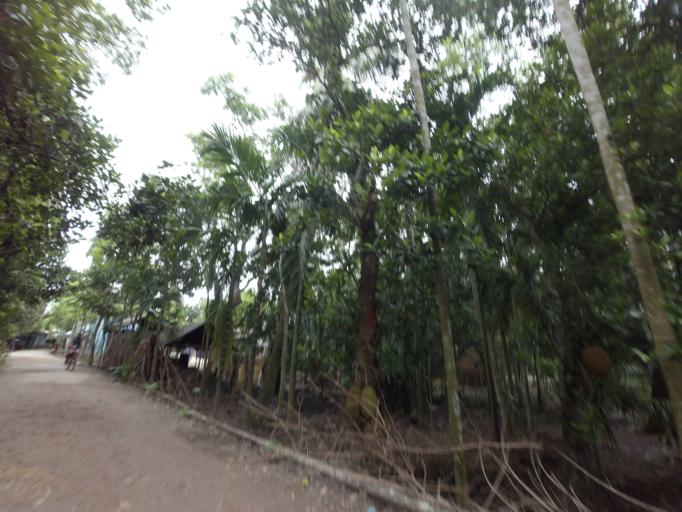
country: BD
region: Khulna
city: Kalia
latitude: 23.0490
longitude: 89.6461
